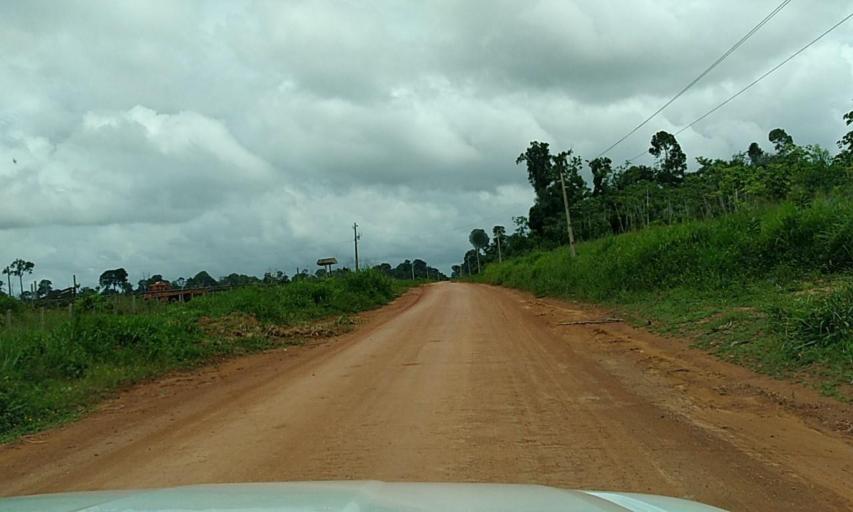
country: BR
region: Para
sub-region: Senador Jose Porfirio
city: Senador Jose Porfirio
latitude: -2.6879
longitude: -51.8273
